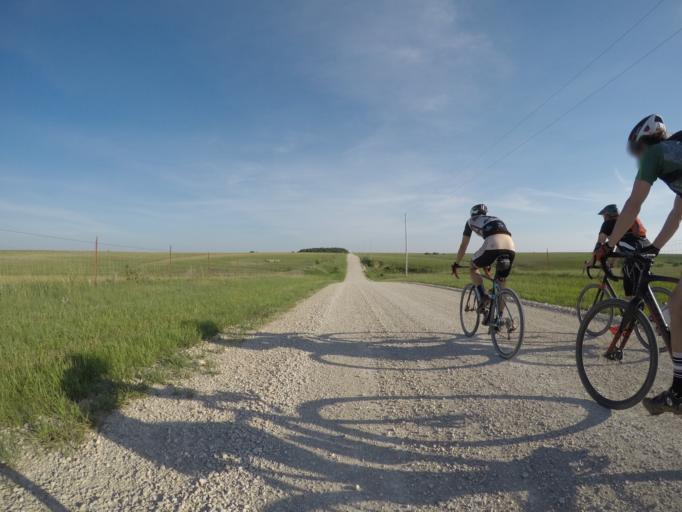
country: US
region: Kansas
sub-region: Riley County
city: Manhattan
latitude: 39.0215
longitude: -96.4918
